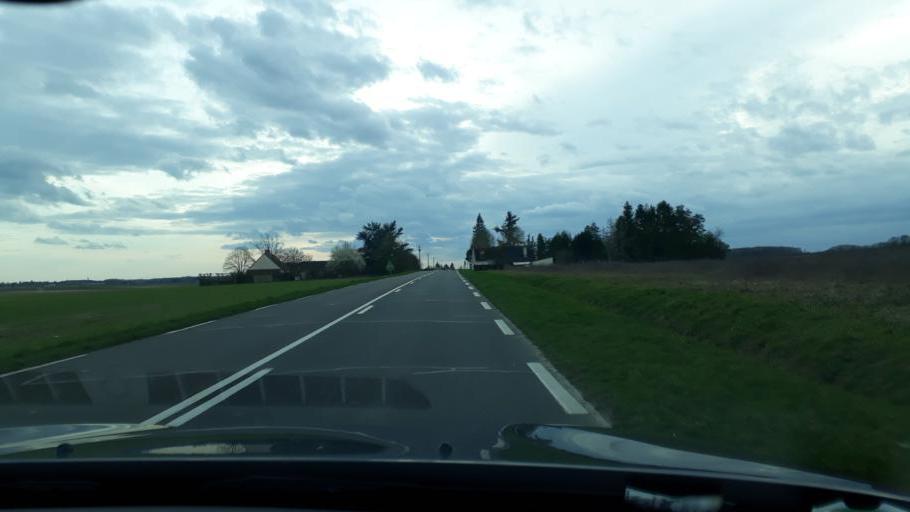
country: FR
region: Centre
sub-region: Departement du Loiret
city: Loury
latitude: 48.0185
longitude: 2.1129
